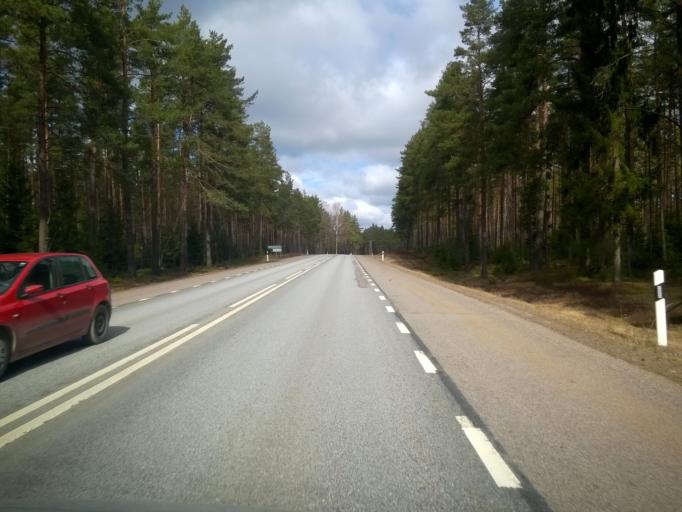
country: SE
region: Uppsala
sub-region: Tierps Kommun
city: Tierp
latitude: 60.1865
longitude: 17.4782
